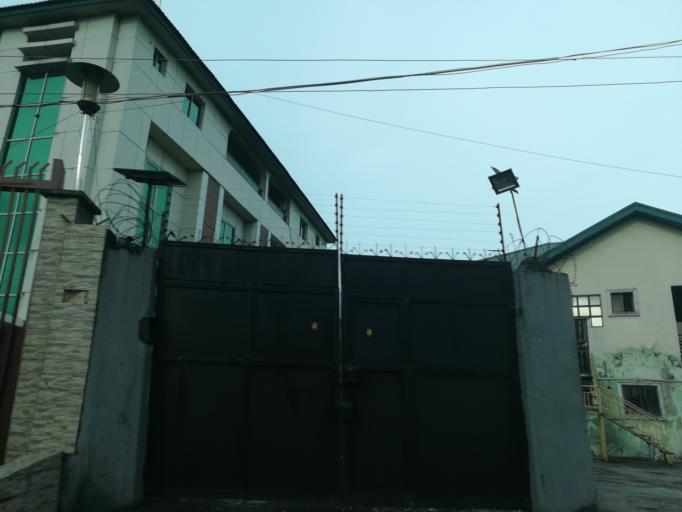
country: NG
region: Rivers
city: Port Harcourt
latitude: 4.8121
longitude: 6.9959
